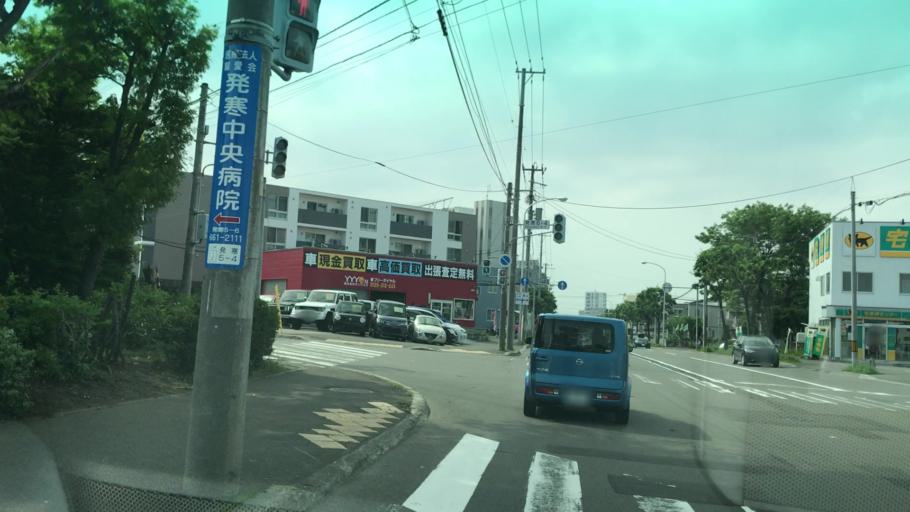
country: JP
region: Hokkaido
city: Sapporo
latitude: 43.0887
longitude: 141.2918
